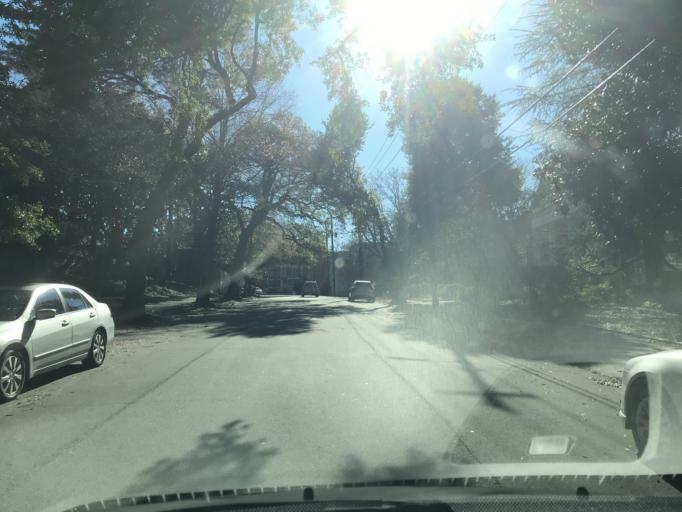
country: US
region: Georgia
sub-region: DeKalb County
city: Druid Hills
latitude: 33.7577
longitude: -84.3561
